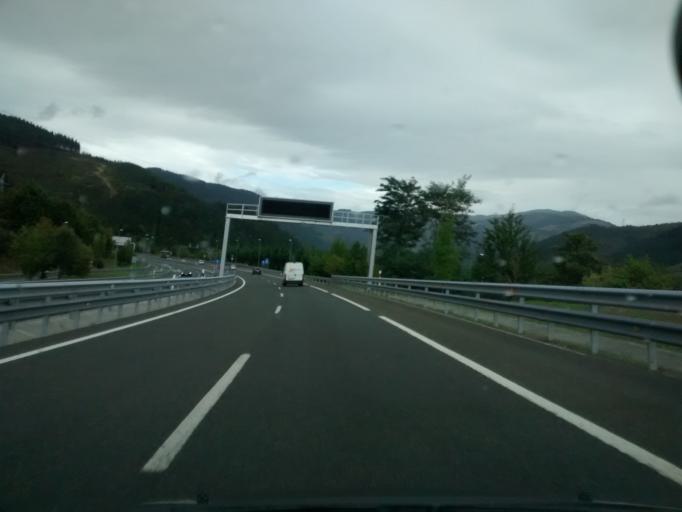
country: ES
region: Basque Country
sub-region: Provincia de Guipuzcoa
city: Bergara
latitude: 43.1288
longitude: -2.4255
